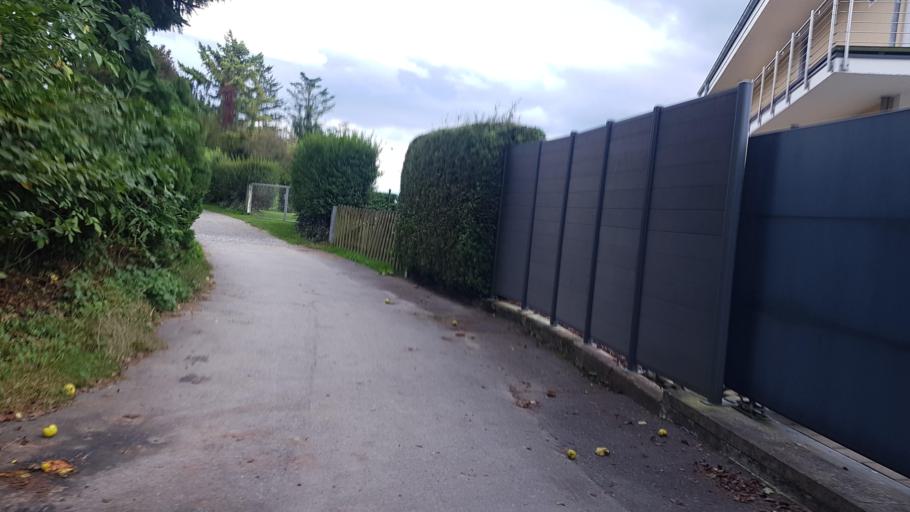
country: DE
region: Baden-Wuerttemberg
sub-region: Tuebingen Region
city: Friedrichshafen
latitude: 47.6582
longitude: 9.4398
